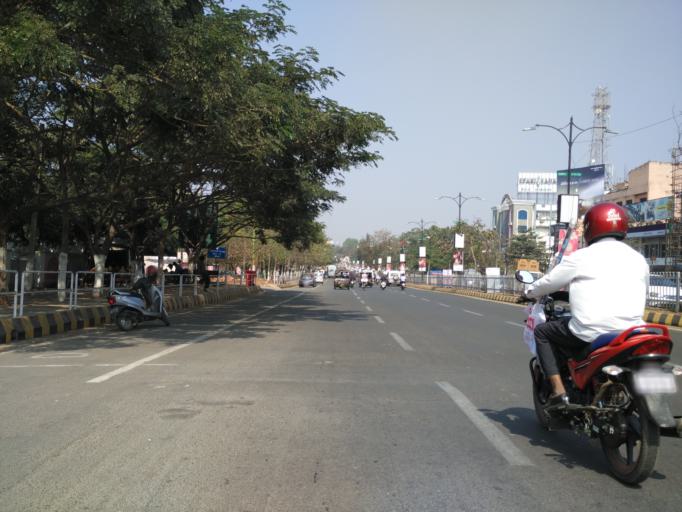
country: IN
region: Odisha
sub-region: Khordha
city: Bhubaneshwar
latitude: 20.2721
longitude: 85.8422
